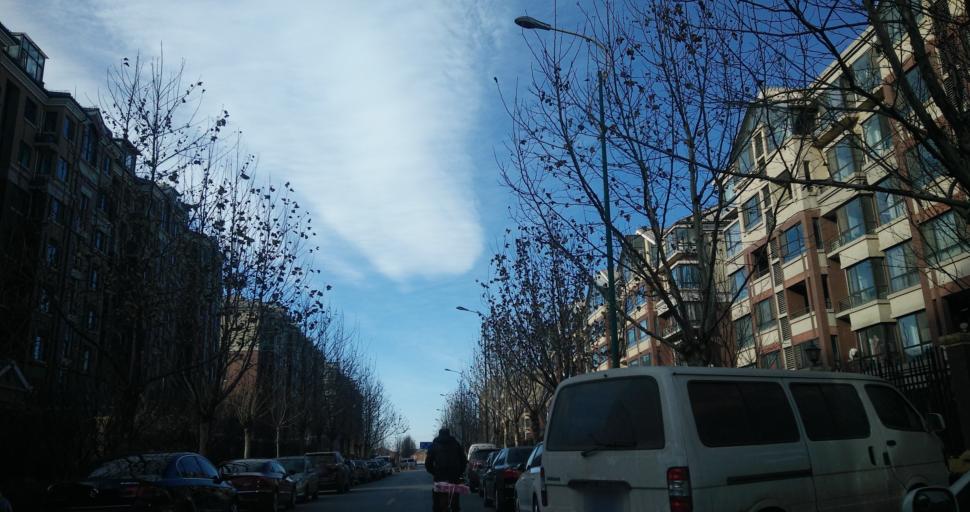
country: CN
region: Beijing
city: Yinghai
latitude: 39.7126
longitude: 116.3954
